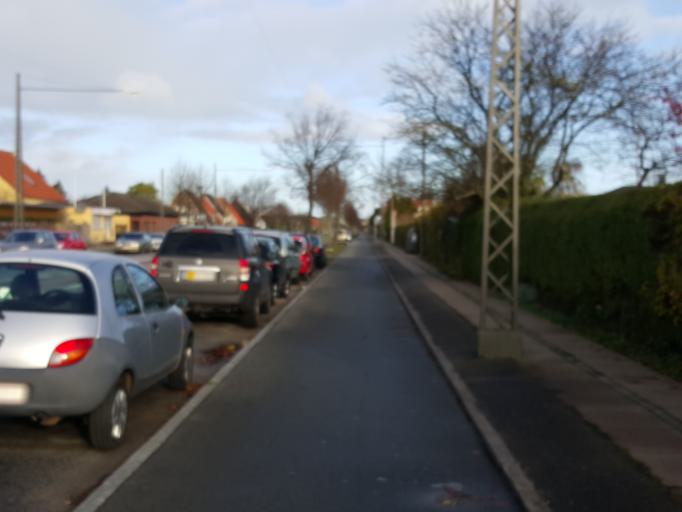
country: DK
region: Capital Region
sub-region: Tarnby Kommune
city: Tarnby
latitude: 55.6322
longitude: 12.5881
